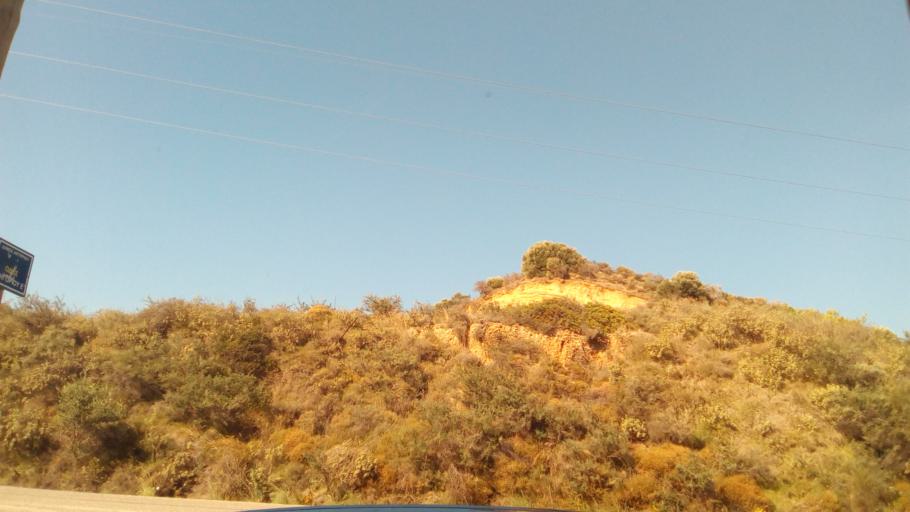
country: GR
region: West Greece
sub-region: Nomos Aitolias kai Akarnanias
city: Antirrio
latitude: 38.3522
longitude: 21.7733
